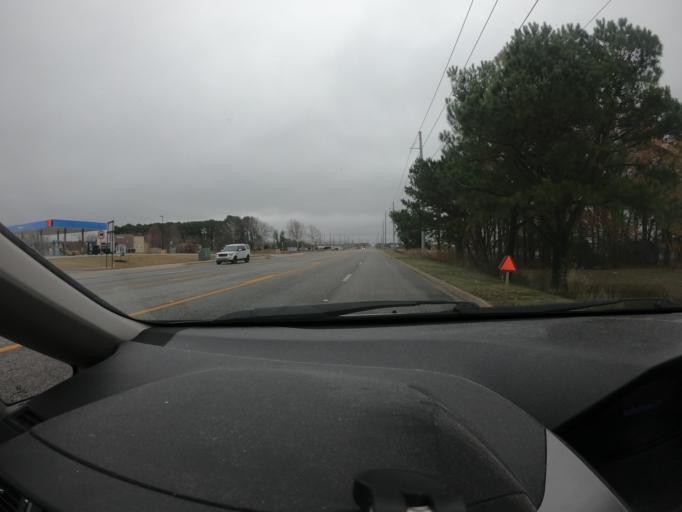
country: US
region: Arkansas
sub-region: Benton County
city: Centerton
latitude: 36.3578
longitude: -94.2528
